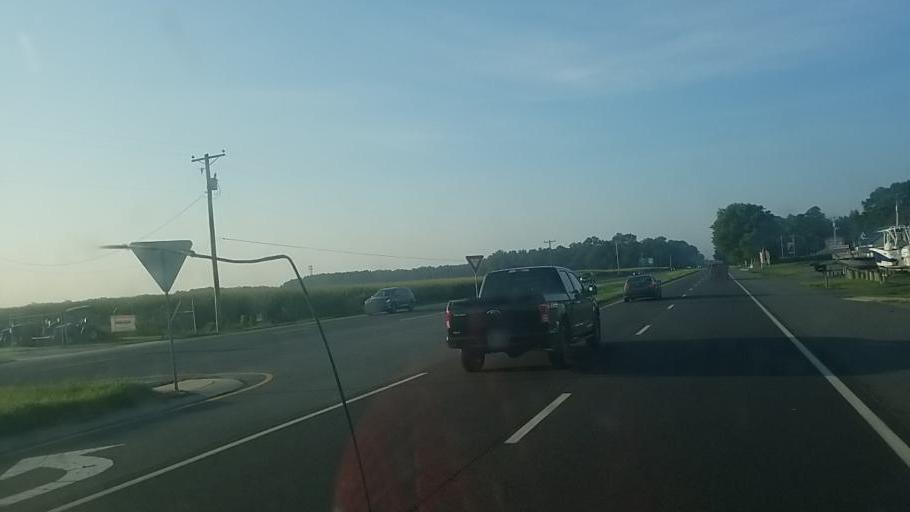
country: US
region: Delaware
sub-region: Sussex County
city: Selbyville
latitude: 38.4782
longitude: -75.2354
